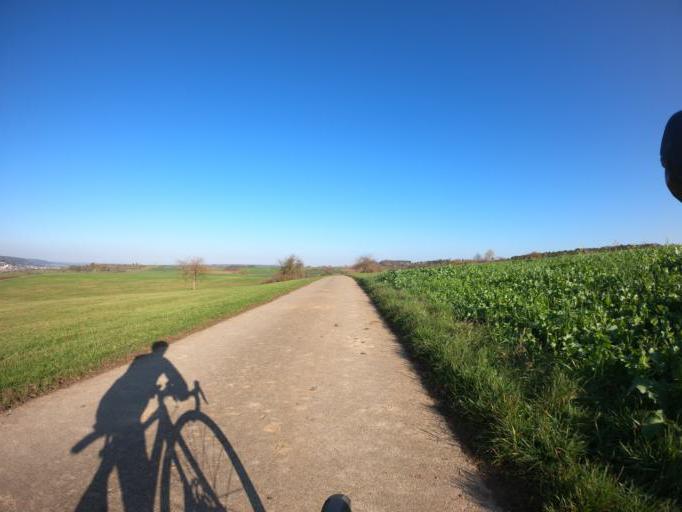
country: DE
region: Baden-Wuerttemberg
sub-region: Regierungsbezirk Stuttgart
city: Weil der Stadt
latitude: 48.7362
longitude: 8.8961
